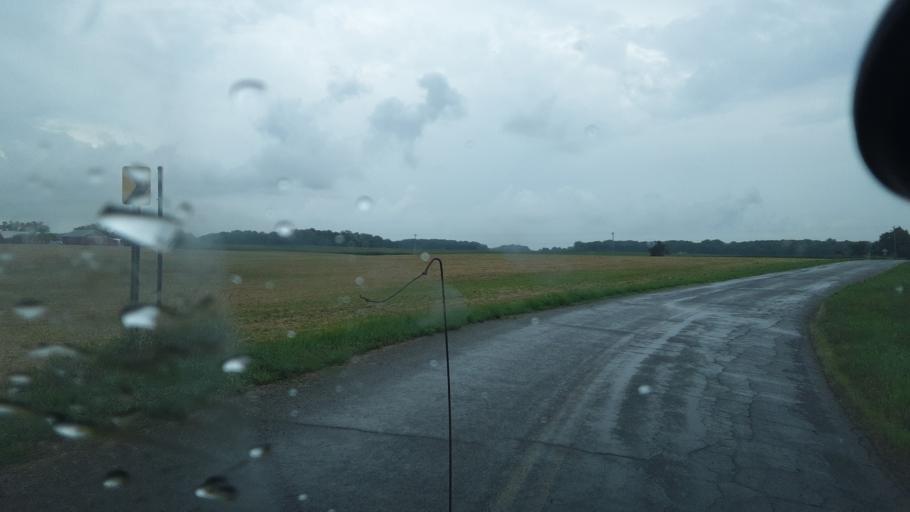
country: US
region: Ohio
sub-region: Williams County
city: Edgerton
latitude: 41.5274
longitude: -84.7912
